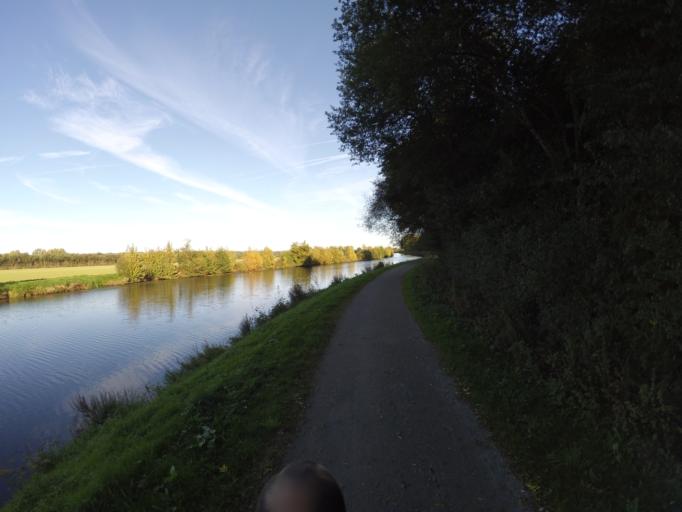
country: FR
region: Brittany
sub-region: Departement du Morbihan
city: Peillac
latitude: 47.7246
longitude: -2.2088
